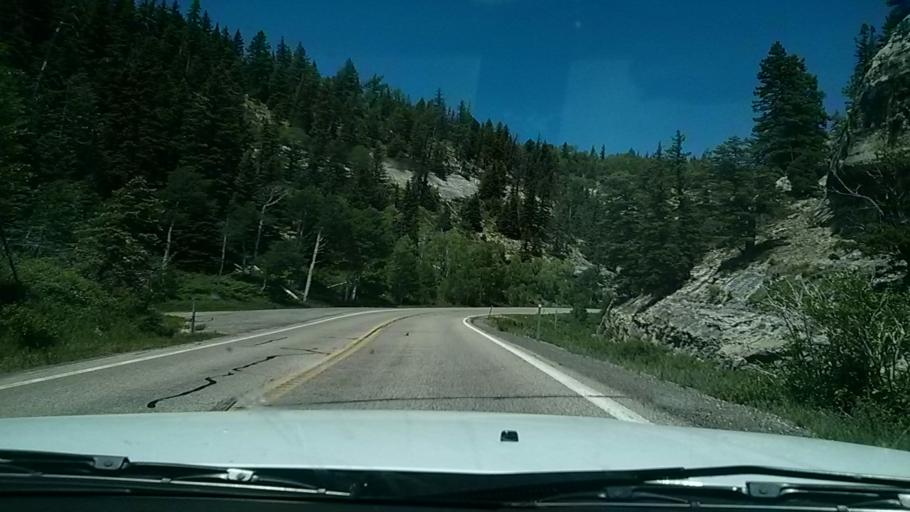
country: US
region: Utah
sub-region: Iron County
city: Cedar City
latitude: 37.6014
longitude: -112.9347
